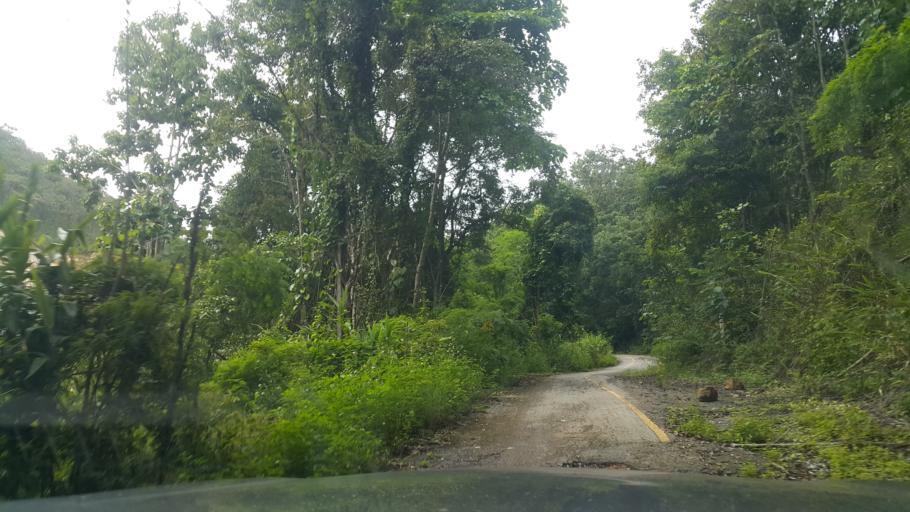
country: TH
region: Chiang Mai
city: San Sai
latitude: 18.9666
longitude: 99.1238
